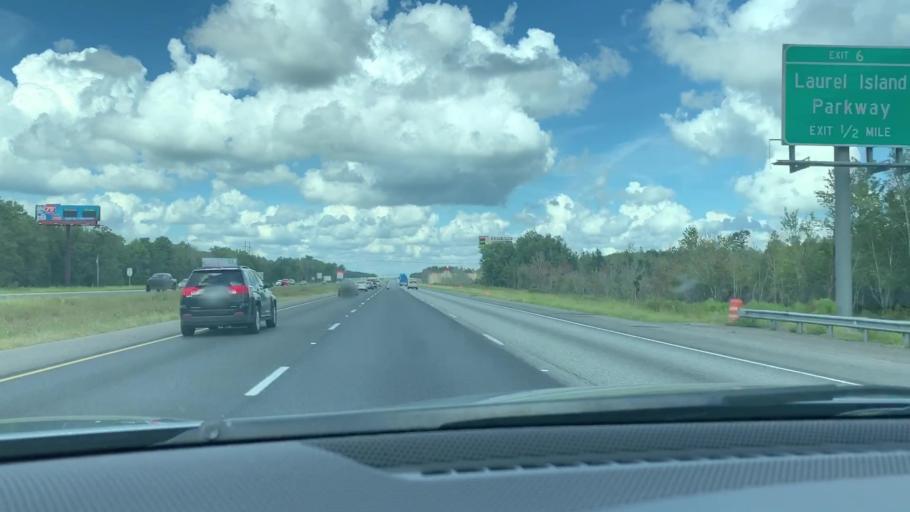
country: US
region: Georgia
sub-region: Camden County
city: Kingsland
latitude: 30.8132
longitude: -81.6638
